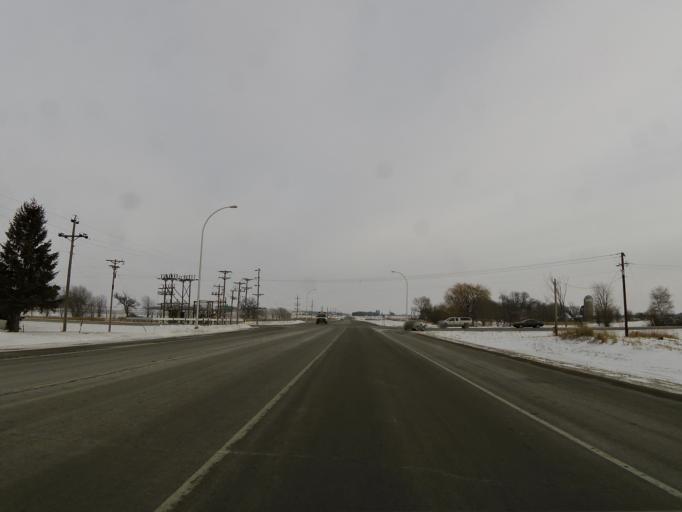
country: US
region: Minnesota
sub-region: McLeod County
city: Lester Prairie
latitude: 44.9062
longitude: -94.0543
